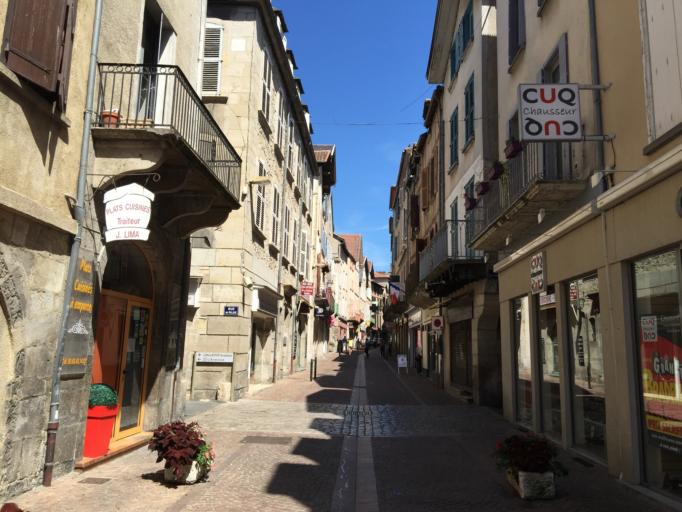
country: FR
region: Midi-Pyrenees
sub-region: Departement de l'Aveyron
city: Villefranche-de-Rouergue
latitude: 44.3499
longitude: 2.0372
